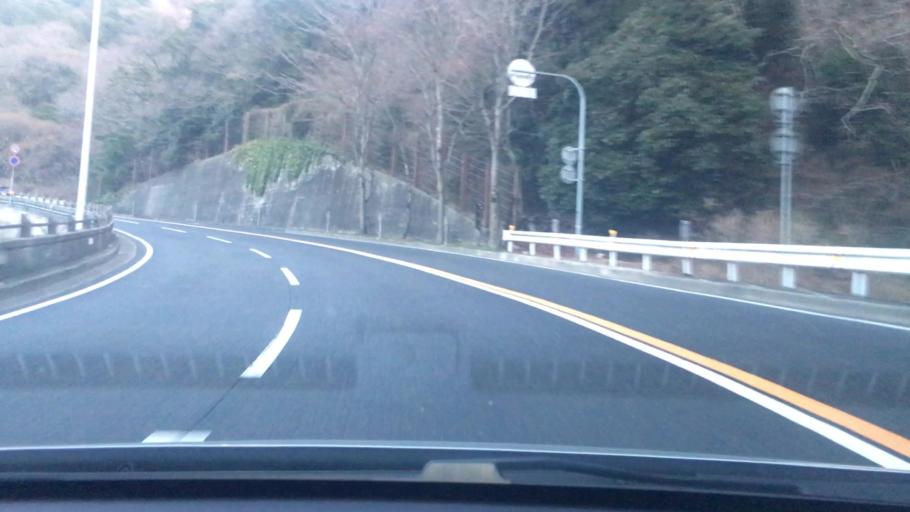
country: JP
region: Hyogo
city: Kobe
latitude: 34.7425
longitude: 135.2304
